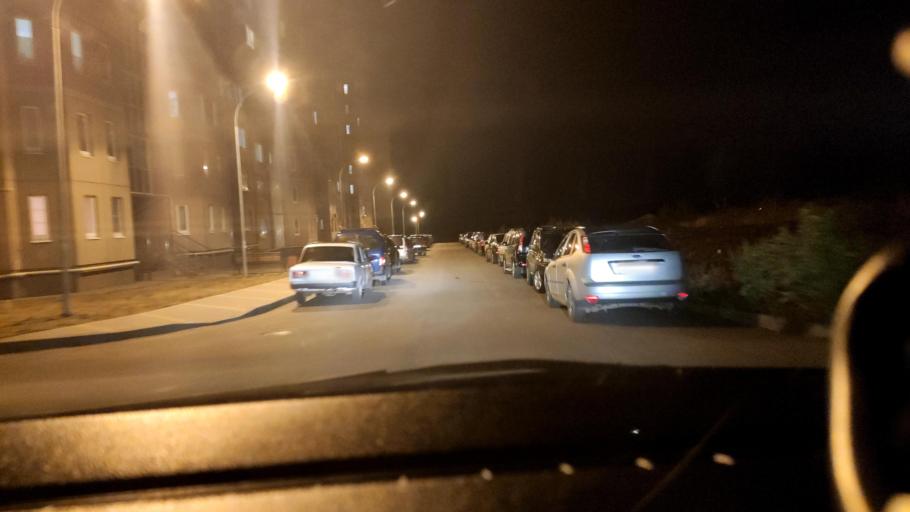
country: RU
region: Voronezj
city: Shilovo
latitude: 51.5734
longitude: 39.1303
